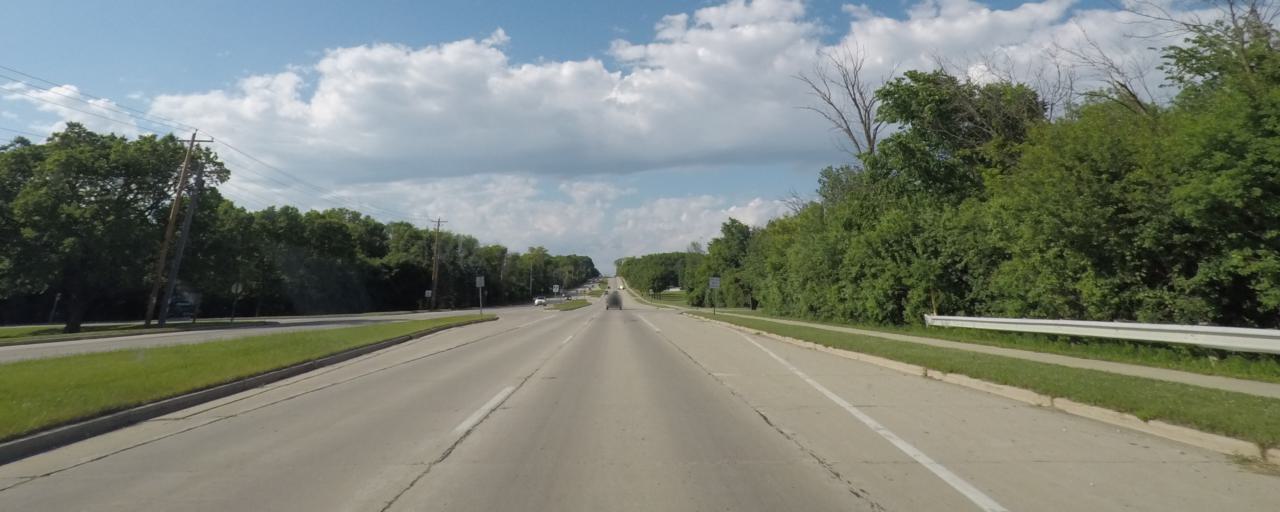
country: US
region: Wisconsin
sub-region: Milwaukee County
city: Greendale
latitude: 42.9283
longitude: -88.0088
